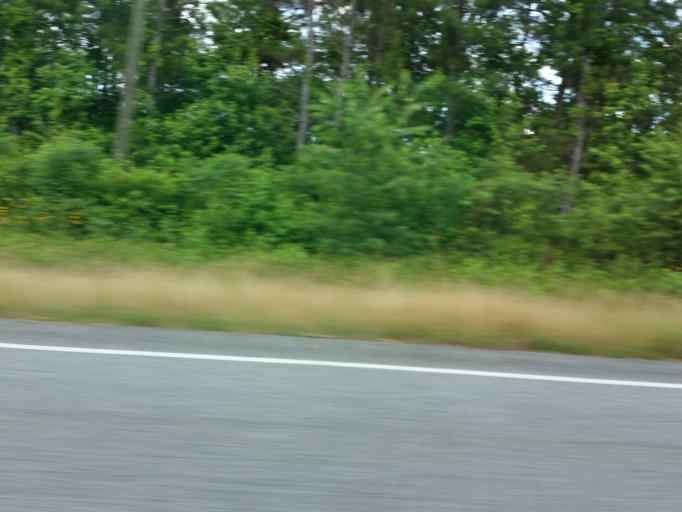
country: US
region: Alabama
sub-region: Sumter County
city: York
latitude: 32.3967
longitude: -88.2100
